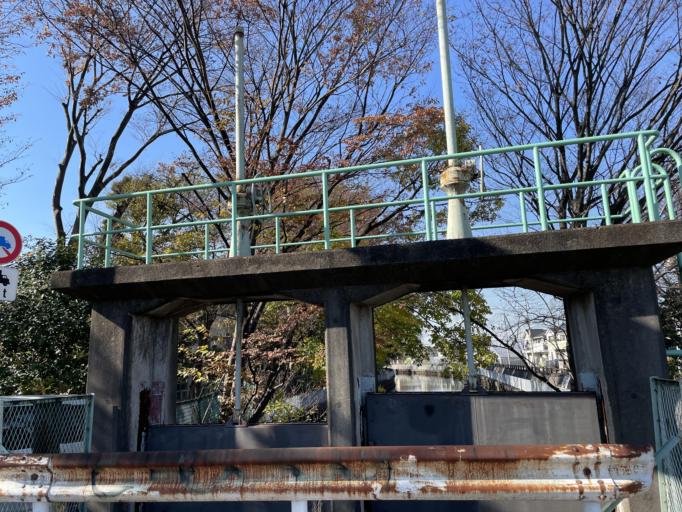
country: JP
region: Saitama
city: Yashio-shi
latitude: 35.8008
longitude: 139.8393
